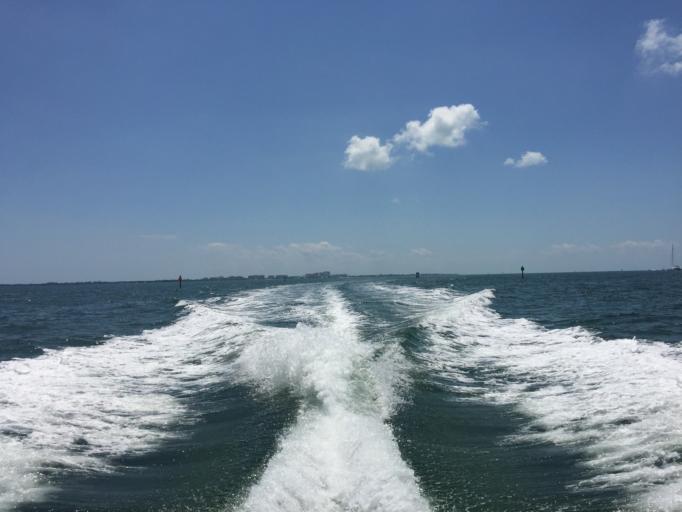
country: US
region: Florida
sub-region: Miami-Dade County
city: Coconut Grove
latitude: 25.7227
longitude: -80.2191
